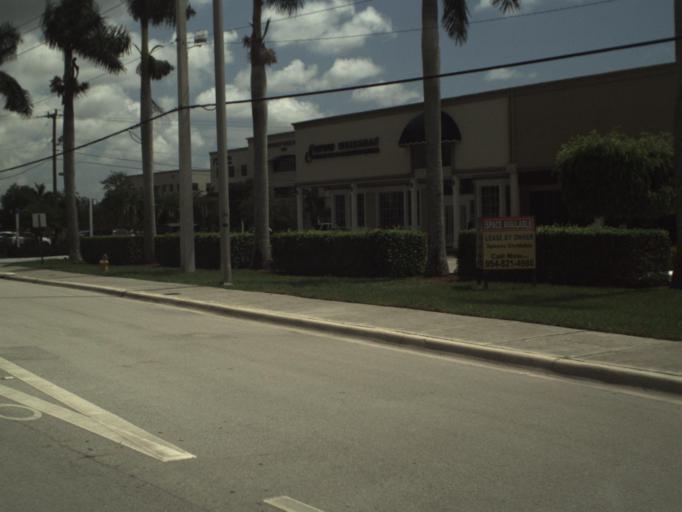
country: US
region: Florida
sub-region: Broward County
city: Margate
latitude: 26.2629
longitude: -80.2015
